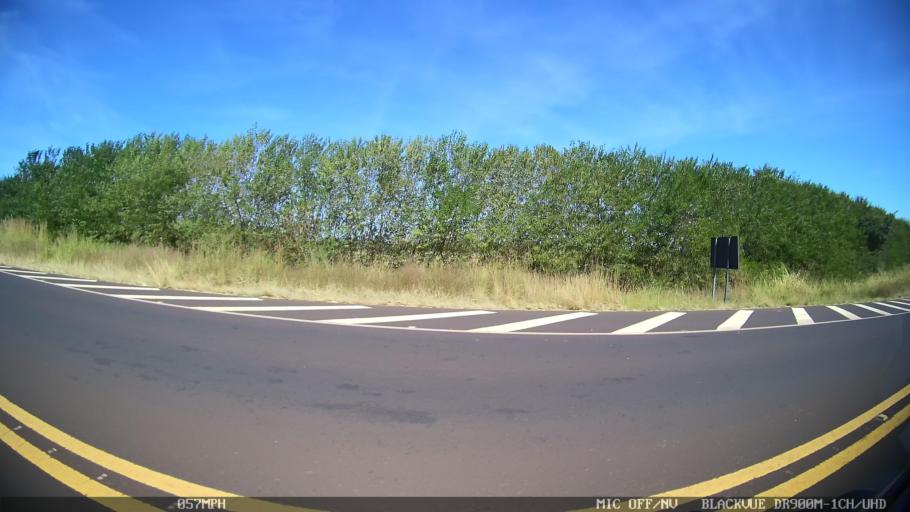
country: BR
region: Sao Paulo
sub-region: Franca
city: Franca
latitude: -20.5596
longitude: -47.5361
